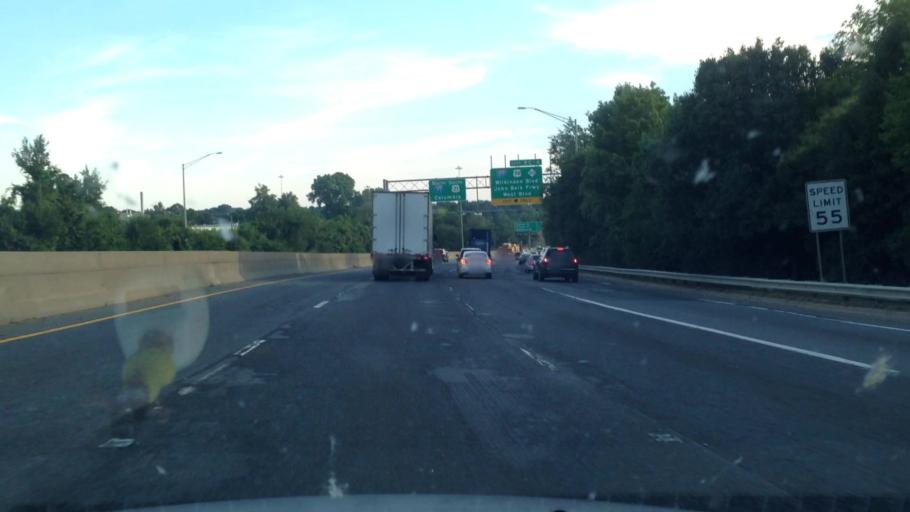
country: US
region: North Carolina
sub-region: Mecklenburg County
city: Charlotte
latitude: 35.2279
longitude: -80.8593
